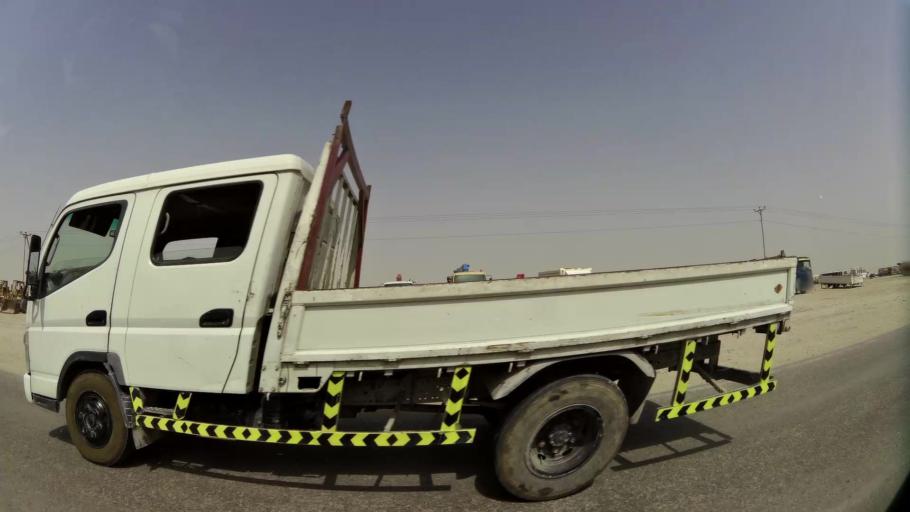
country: QA
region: Baladiyat ar Rayyan
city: Ar Rayyan
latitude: 25.2087
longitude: 51.3601
